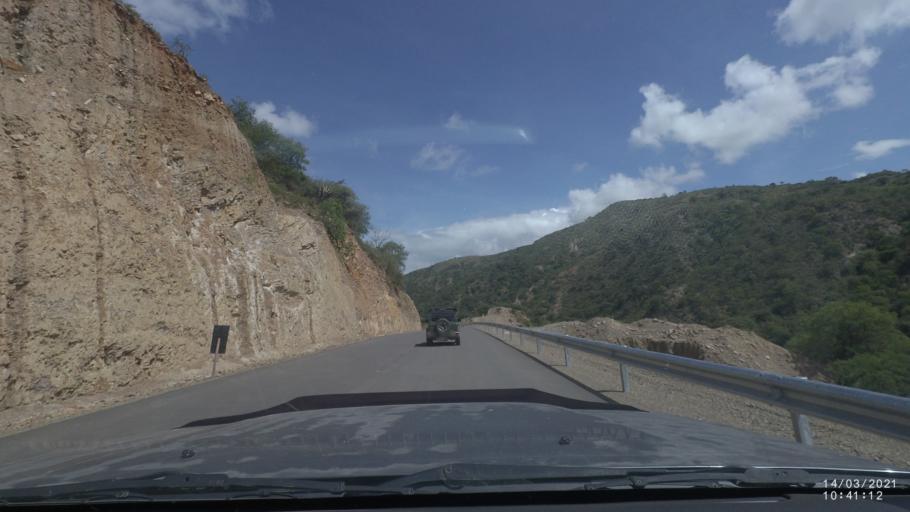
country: BO
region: Cochabamba
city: Tarata
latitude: -17.8804
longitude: -65.9099
